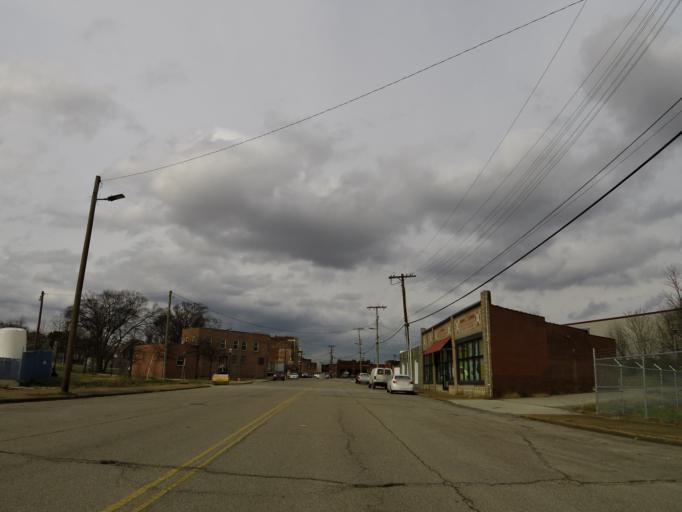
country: US
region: Tennessee
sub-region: Hamilton County
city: Chattanooga
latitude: 35.0327
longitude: -85.3038
